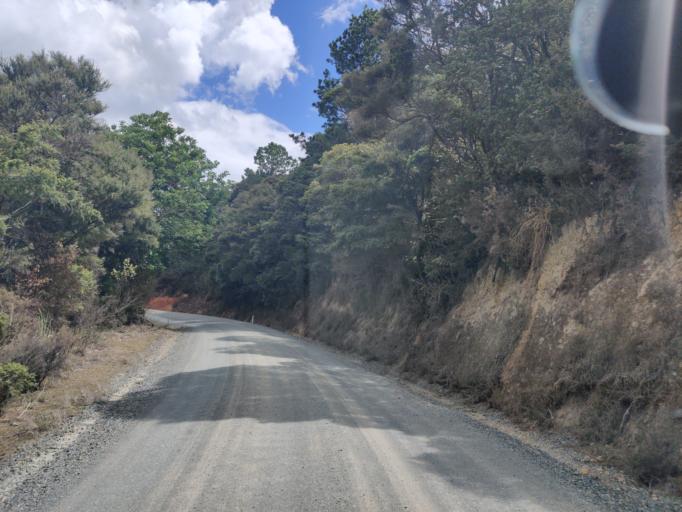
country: NZ
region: Northland
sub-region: Far North District
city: Paihia
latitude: -35.2607
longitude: 174.0498
